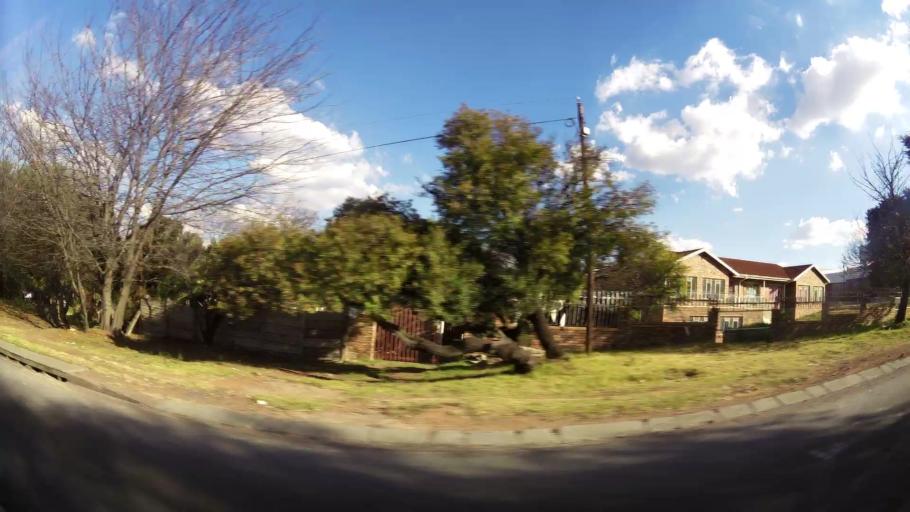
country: ZA
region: Mpumalanga
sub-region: Nkangala District Municipality
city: Witbank
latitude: -25.8765
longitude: 29.2433
